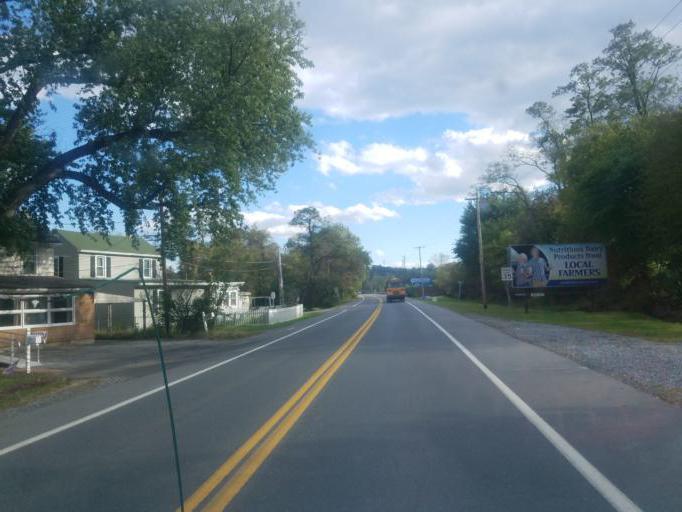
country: US
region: Pennsylvania
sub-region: Dauphin County
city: Middletown
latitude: 40.1854
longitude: -76.7281
